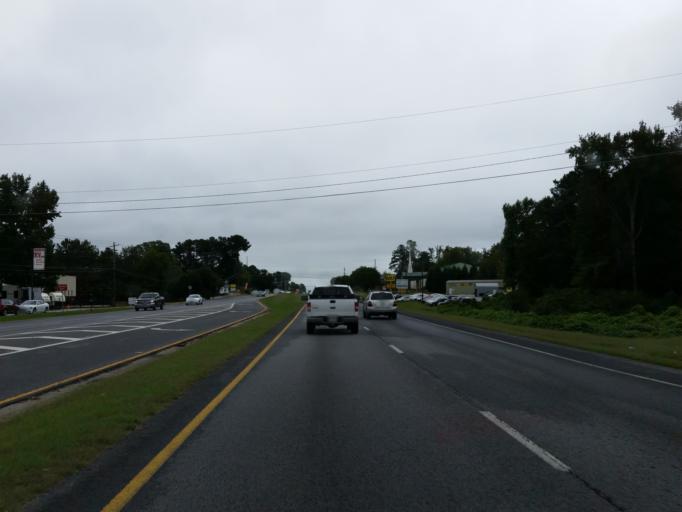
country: US
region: Georgia
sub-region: Clayton County
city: Irondale
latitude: 33.4918
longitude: -84.3421
